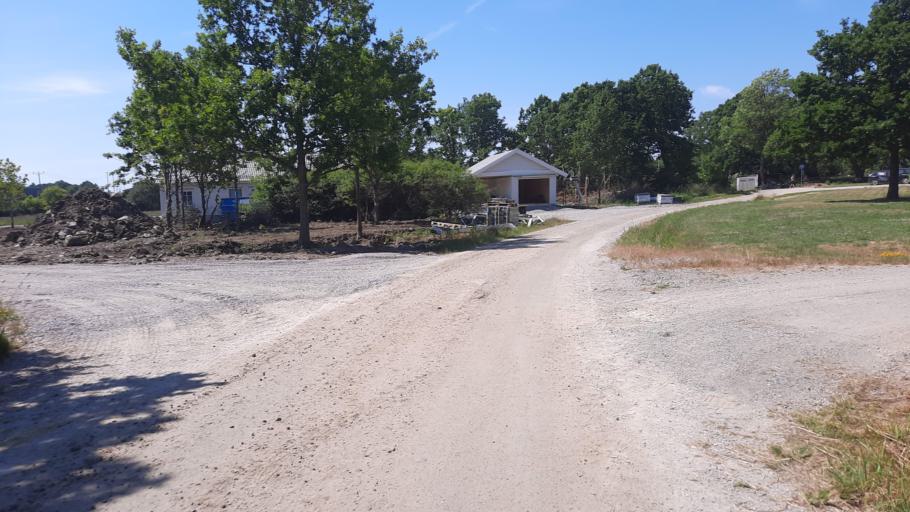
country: SE
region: Blekinge
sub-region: Karlskrona Kommun
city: Jaemjoe
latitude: 56.1493
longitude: 15.7555
